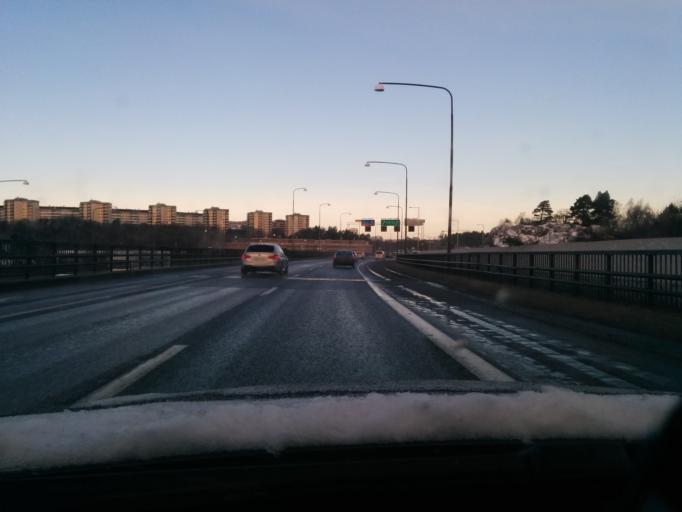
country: SE
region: Stockholm
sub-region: Solna Kommun
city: Solna
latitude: 59.3415
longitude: 18.0104
